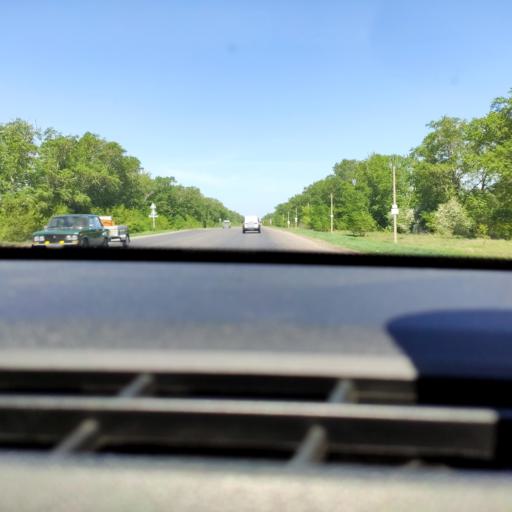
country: RU
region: Samara
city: Tol'yatti
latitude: 53.5895
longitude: 49.4060
